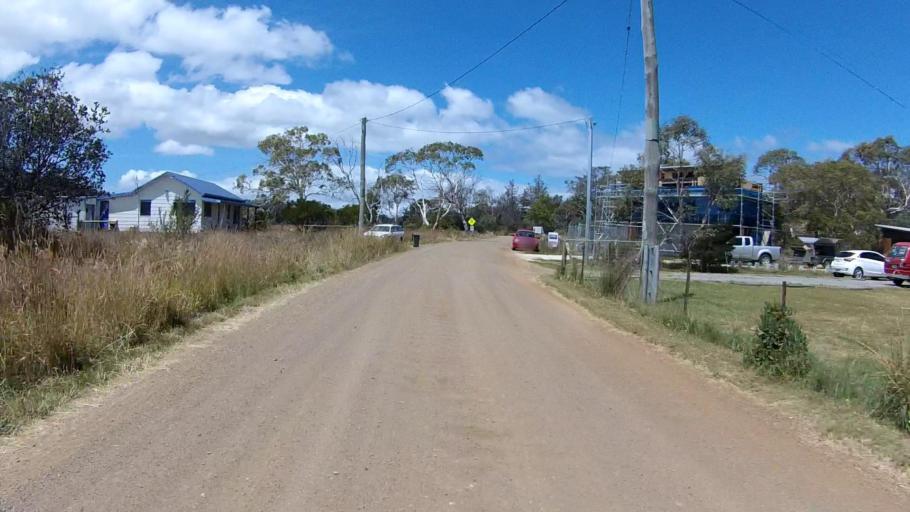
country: AU
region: Tasmania
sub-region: Sorell
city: Sorell
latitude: -42.8726
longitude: 147.6426
